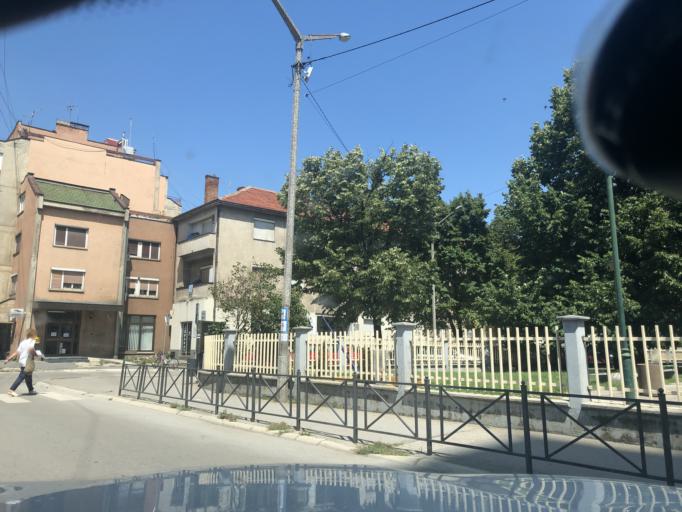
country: RS
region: Central Serbia
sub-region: Jablanicki Okrug
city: Leskovac
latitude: 42.9944
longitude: 21.9480
